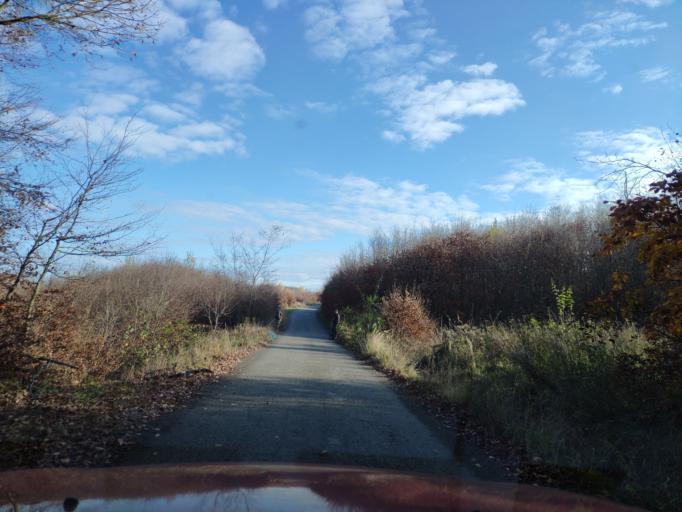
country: SK
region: Kosicky
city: Kosice
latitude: 48.6273
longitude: 21.4553
